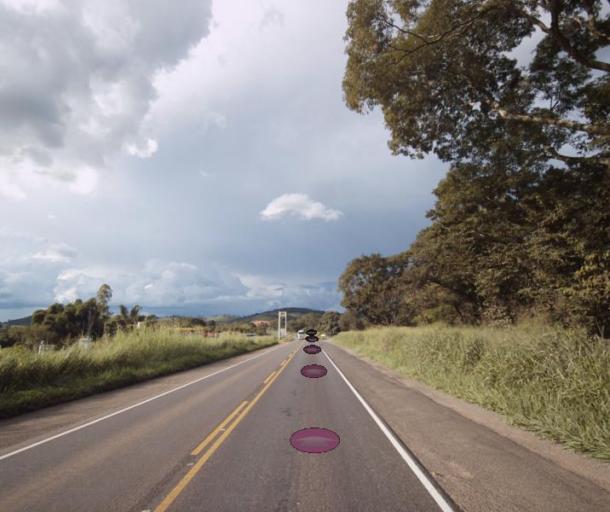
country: BR
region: Goias
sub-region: Rialma
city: Rialma
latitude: -15.2769
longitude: -49.5524
